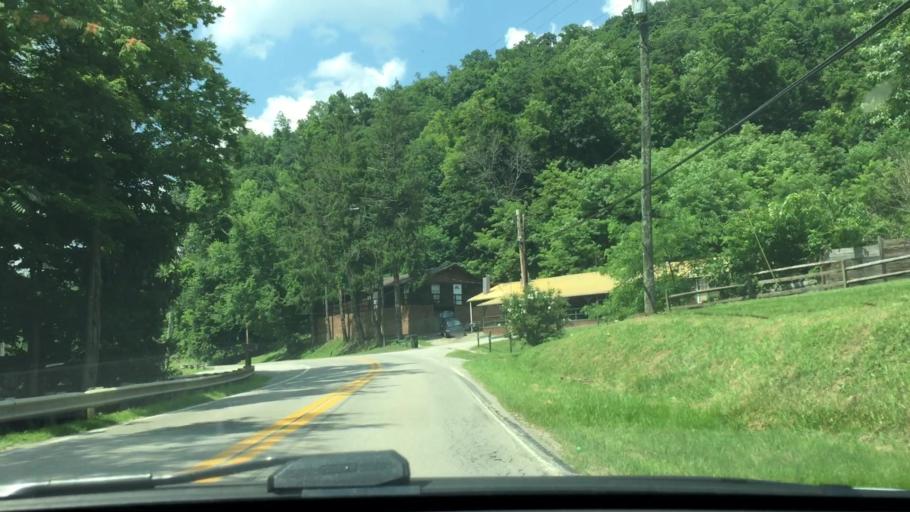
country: US
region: West Virginia
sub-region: Wetzel County
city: New Martinsville
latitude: 39.7059
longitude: -80.8192
